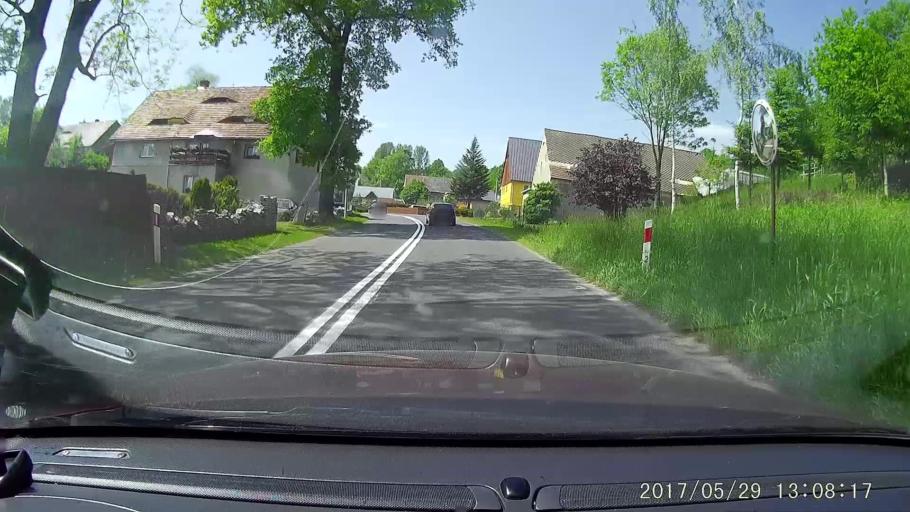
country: PL
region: Lower Silesian Voivodeship
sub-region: Powiat jeleniogorski
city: Stara Kamienica
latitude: 50.9608
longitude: 15.5621
